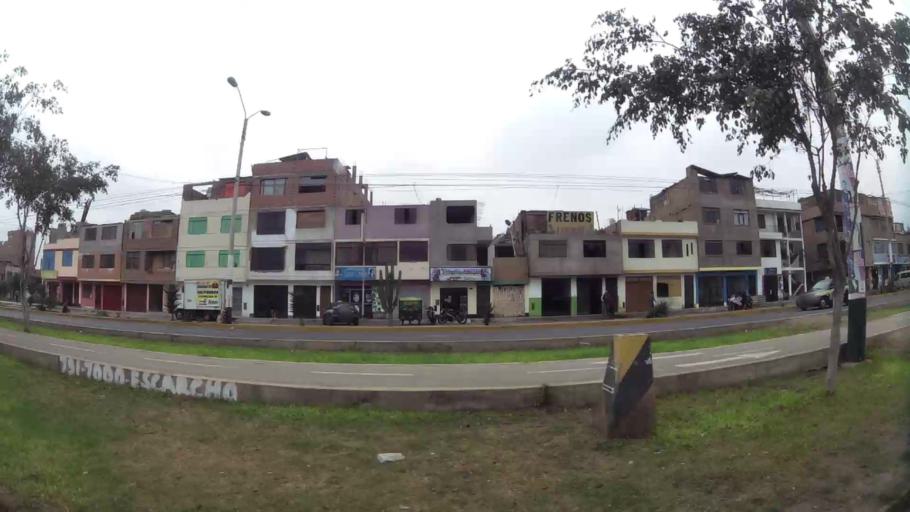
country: PE
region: Lima
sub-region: Lima
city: Independencia
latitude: -11.9834
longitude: -77.0767
